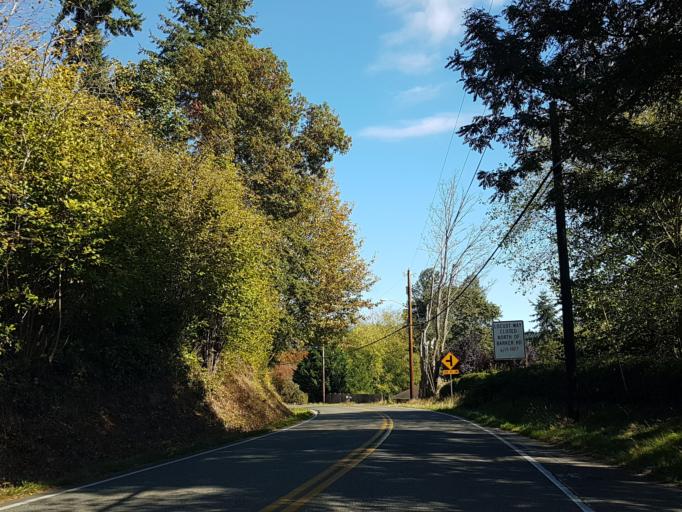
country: US
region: Washington
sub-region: Snohomish County
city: Brier
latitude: 47.7789
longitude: -122.2588
